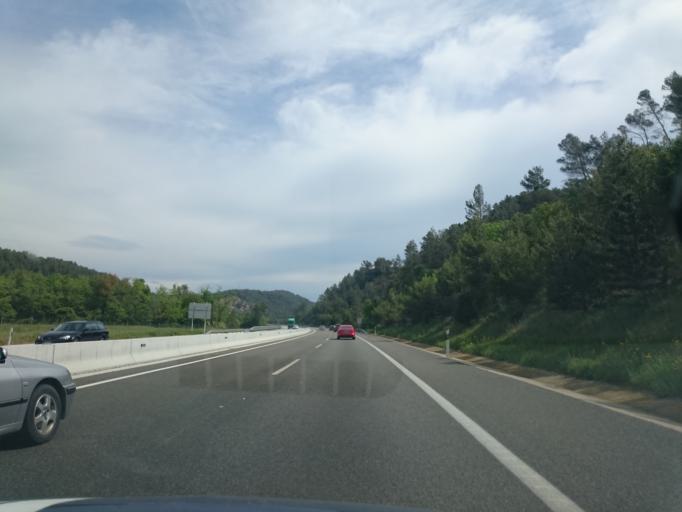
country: ES
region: Catalonia
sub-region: Provincia de Barcelona
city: Avinyo
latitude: 41.8356
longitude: 1.9777
